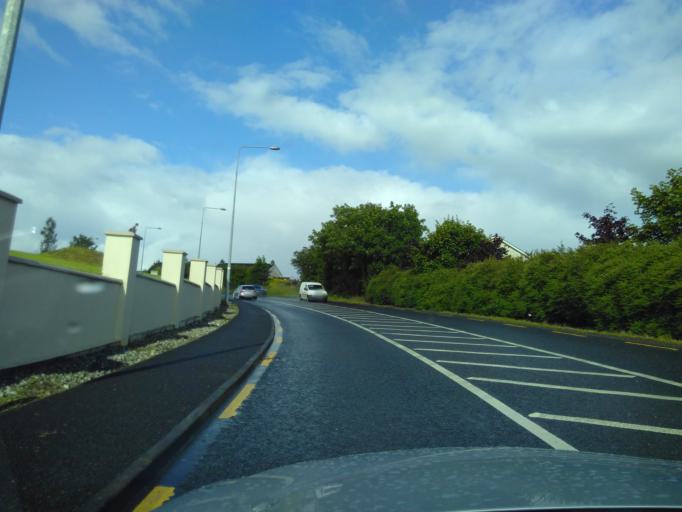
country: IE
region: Ulster
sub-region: County Donegal
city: Letterkenny
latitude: 54.9584
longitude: -7.6938
